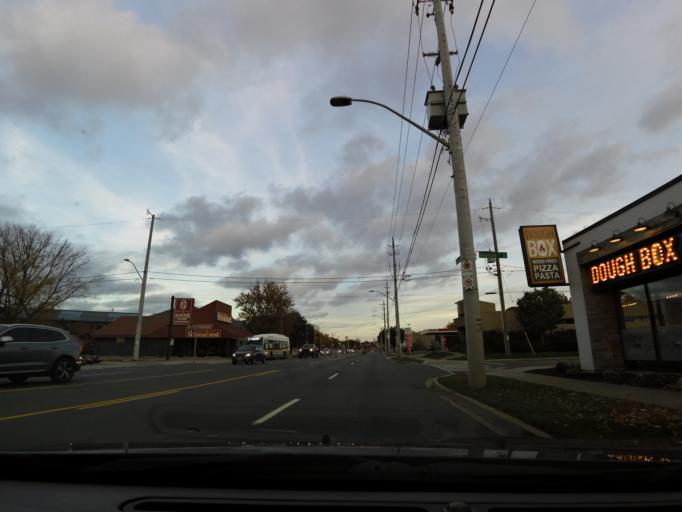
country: CA
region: Ontario
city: Ancaster
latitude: 43.2576
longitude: -79.9241
